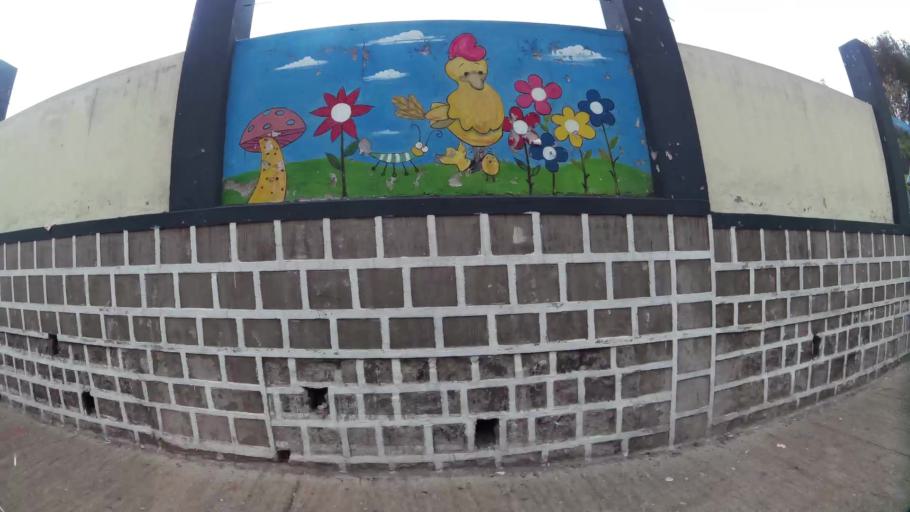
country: EC
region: Pichincha
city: Sangolqui
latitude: -0.3330
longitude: -78.4521
